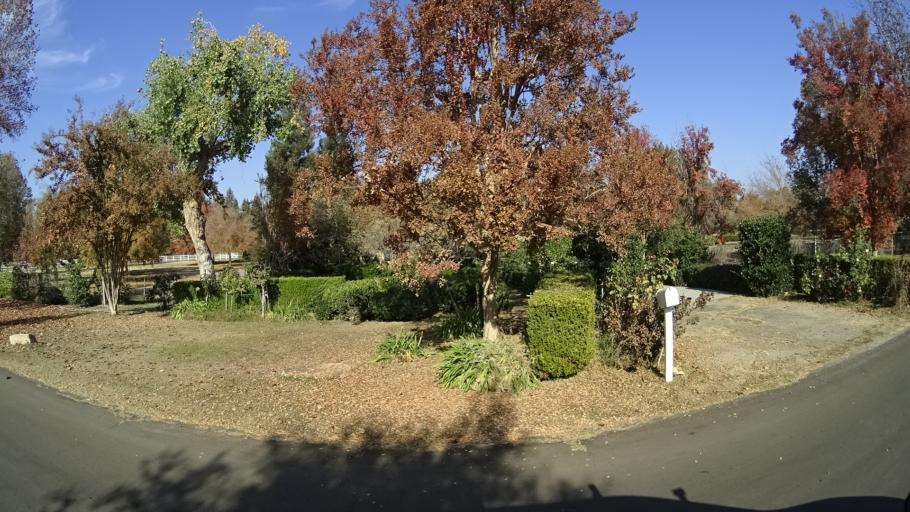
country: US
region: California
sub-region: Kern County
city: Rosedale
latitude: 35.3617
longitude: -119.1820
